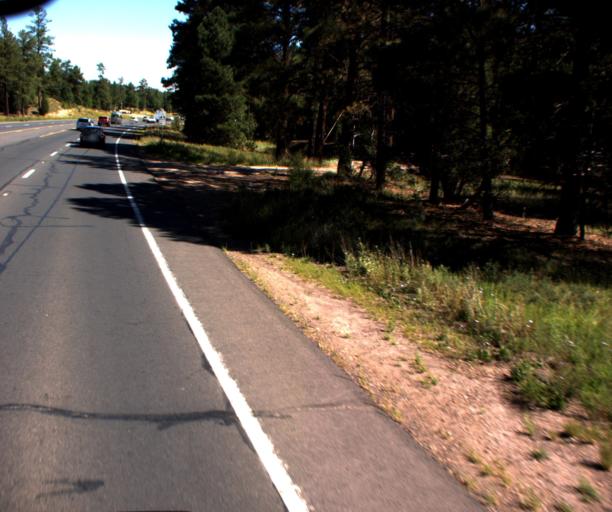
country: US
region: Arizona
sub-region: Navajo County
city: Show Low
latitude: 34.2227
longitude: -110.0294
